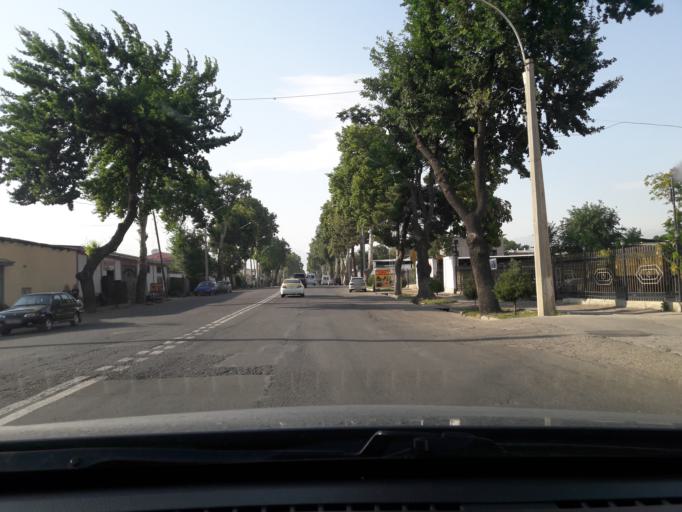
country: TJ
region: Dushanbe
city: Dushanbe
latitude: 38.5356
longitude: 68.7718
